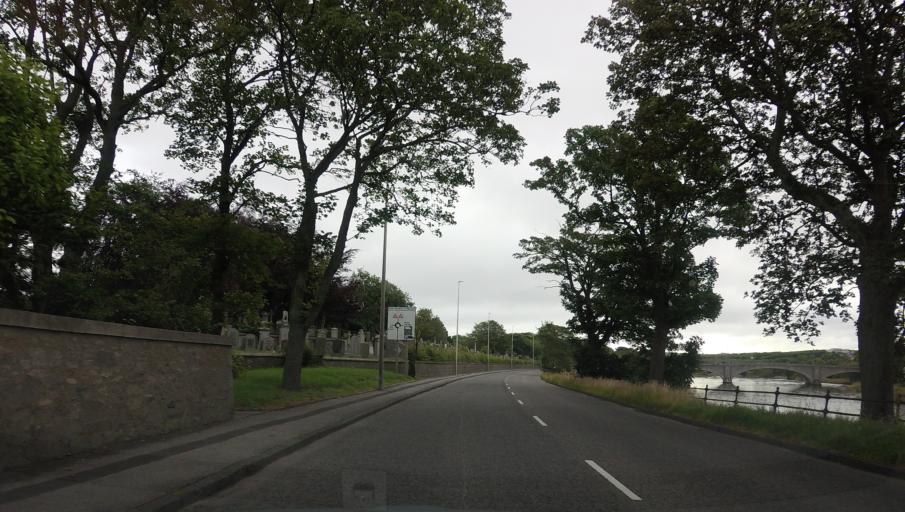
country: GB
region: Scotland
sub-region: Aberdeen City
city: Aberdeen
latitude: 57.1294
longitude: -2.1120
